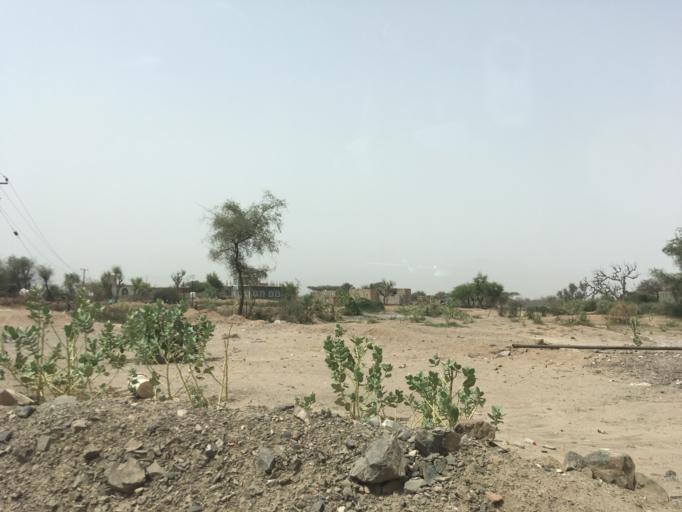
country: YE
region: Ad Dali'
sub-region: Qa'atabah
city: Qa`tabah
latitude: 13.8302
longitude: 44.7429
